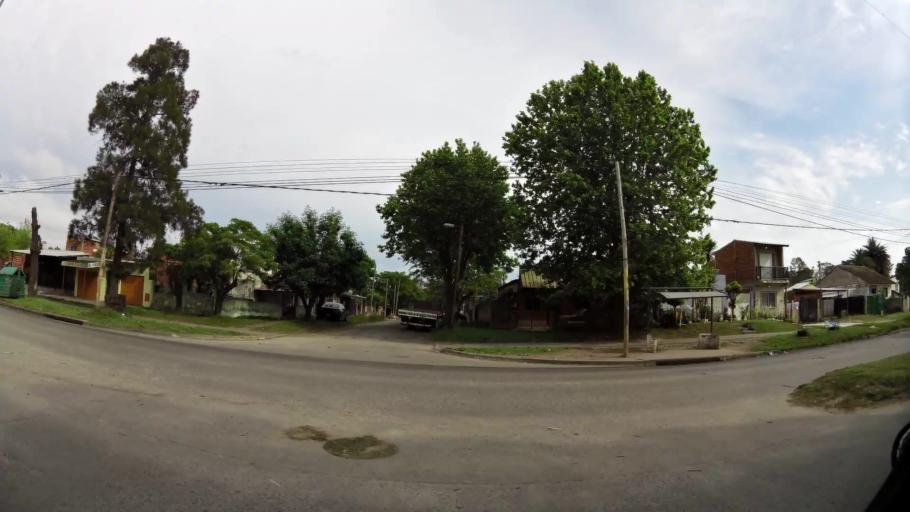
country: AR
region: Buenos Aires
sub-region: Partido de Quilmes
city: Quilmes
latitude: -34.7104
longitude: -58.2365
